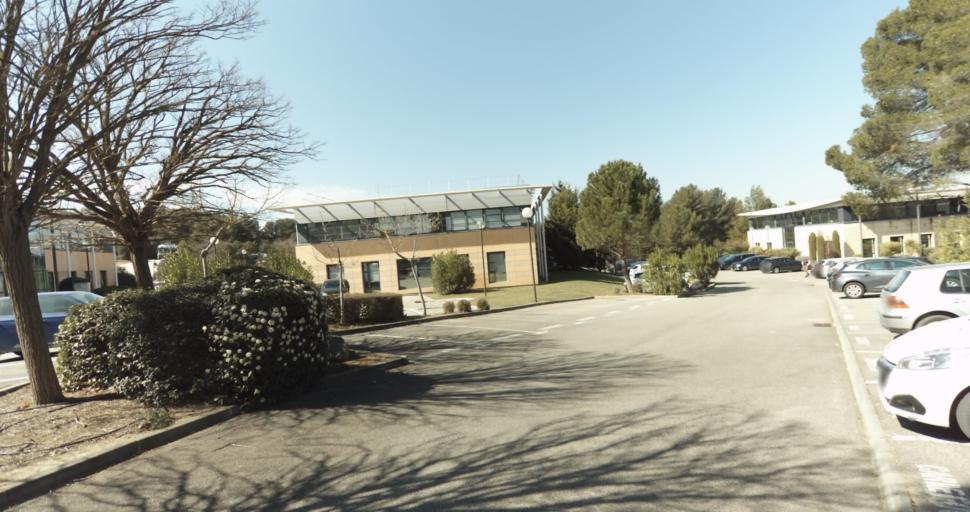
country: FR
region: Provence-Alpes-Cote d'Azur
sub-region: Departement des Bouches-du-Rhone
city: Cabries
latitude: 43.4772
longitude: 5.3682
